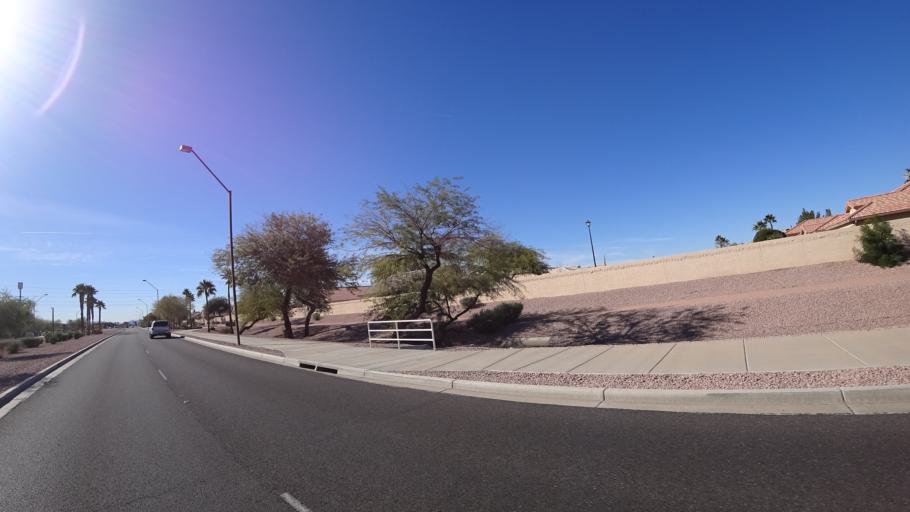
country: US
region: Arizona
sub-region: Maricopa County
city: Litchfield Park
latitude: 33.4806
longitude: -112.3926
